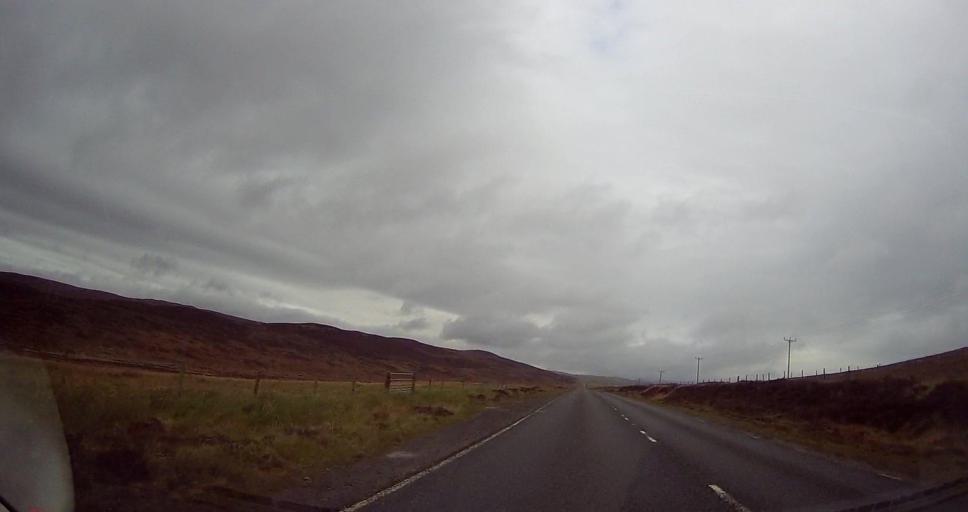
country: GB
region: Scotland
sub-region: Shetland Islands
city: Lerwick
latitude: 60.2033
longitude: -1.2331
